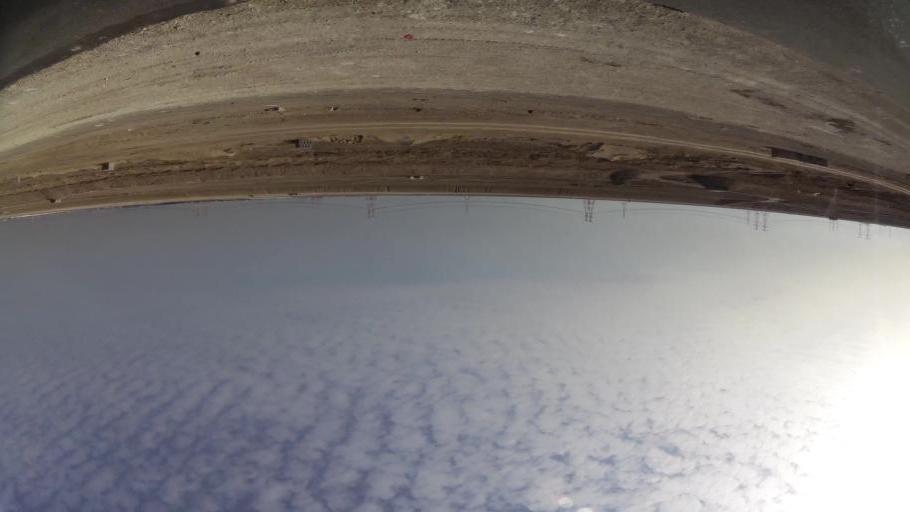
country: AE
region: Abu Dhabi
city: Abu Dhabi
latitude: 24.2334
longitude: 54.4581
